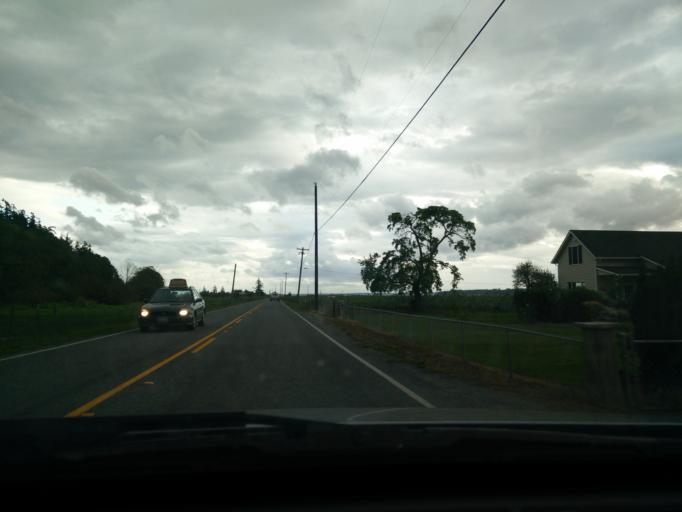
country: US
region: Washington
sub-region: Snohomish County
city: Stanwood
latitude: 48.2692
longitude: -122.3666
